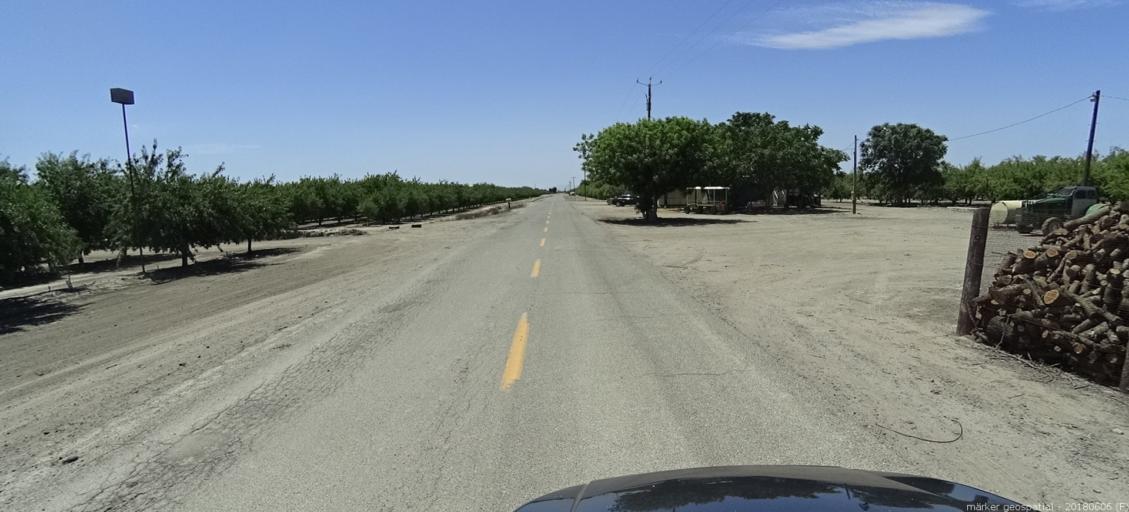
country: US
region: California
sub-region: Fresno County
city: Firebaugh
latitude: 36.8515
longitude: -120.3909
